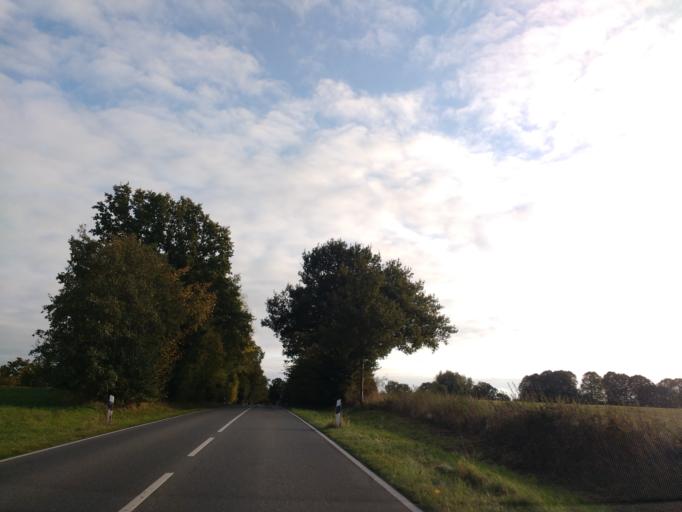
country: DE
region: Schleswig-Holstein
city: Altenkrempe
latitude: 54.1428
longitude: 10.8220
